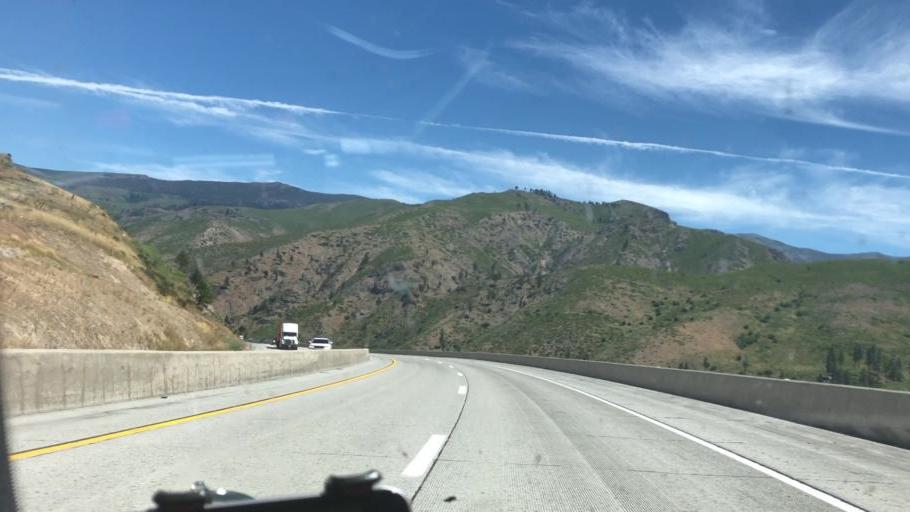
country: US
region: California
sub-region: Placer County
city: Tahoe Vista
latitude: 39.3696
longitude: -120.0470
